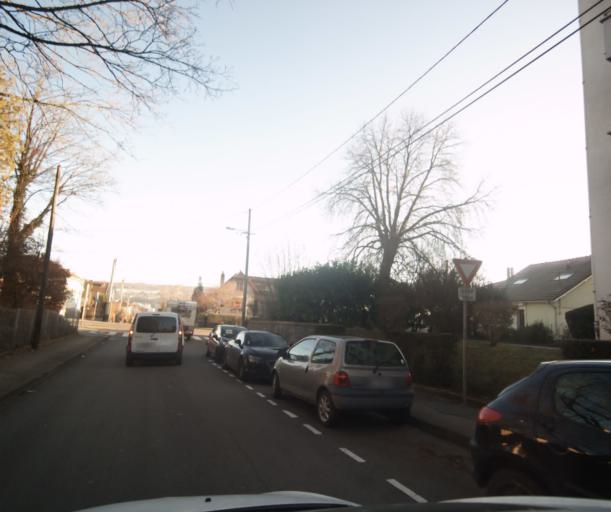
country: FR
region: Franche-Comte
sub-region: Departement du Doubs
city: Besancon
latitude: 47.2574
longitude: 6.0354
